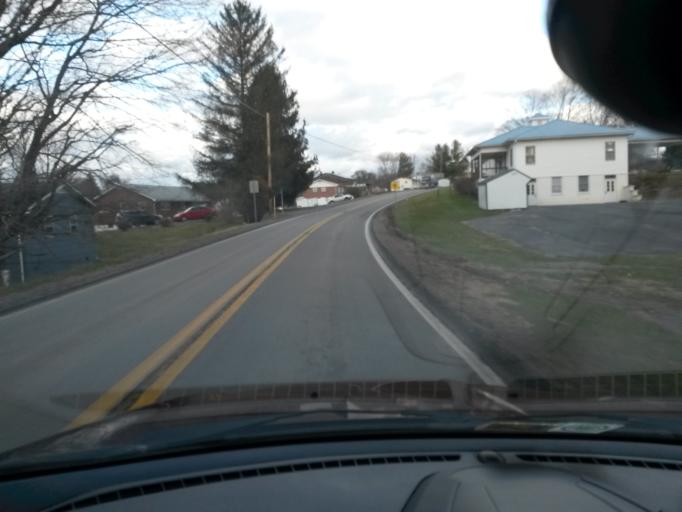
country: US
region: West Virginia
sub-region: Monroe County
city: Union
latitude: 37.5892
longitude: -80.5477
